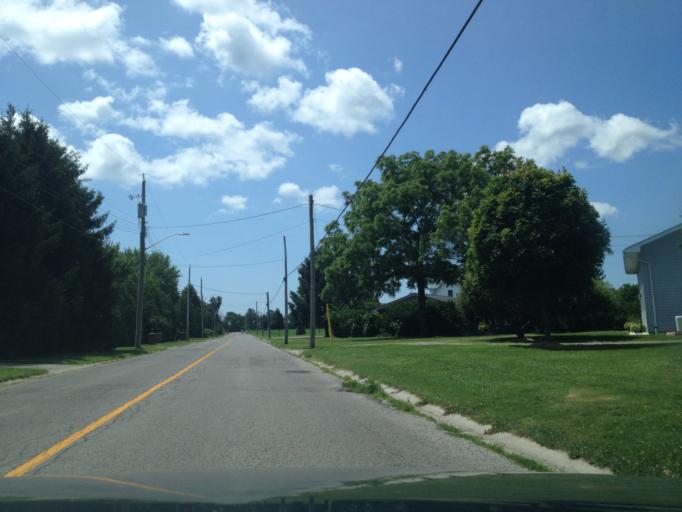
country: CA
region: Ontario
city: Norfolk County
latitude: 42.6335
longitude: -80.4421
